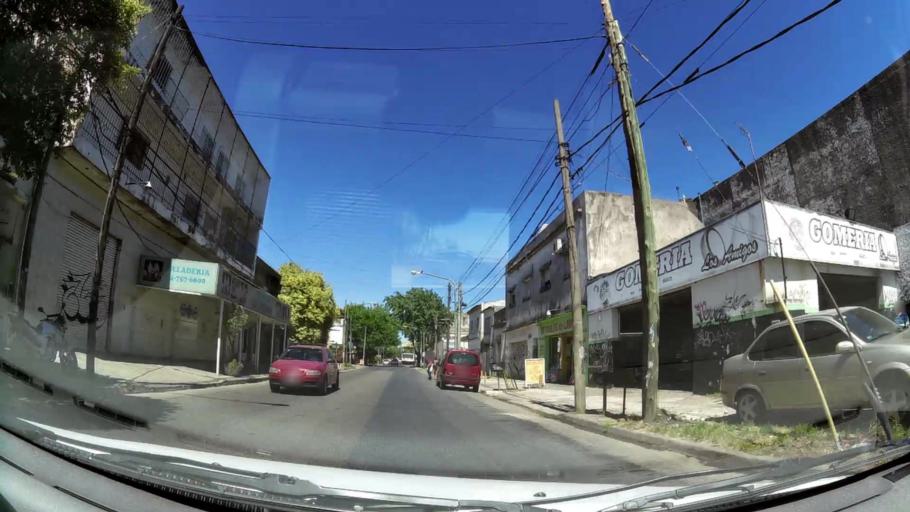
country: AR
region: Buenos Aires
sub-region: Partido de General San Martin
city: General San Martin
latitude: -34.5922
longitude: -58.5339
